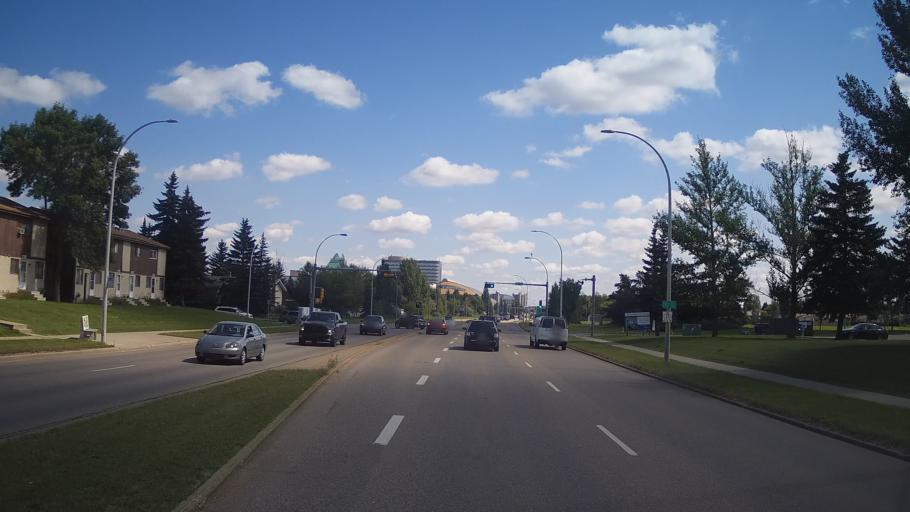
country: CA
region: Alberta
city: St. Albert
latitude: 53.5216
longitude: -113.6387
